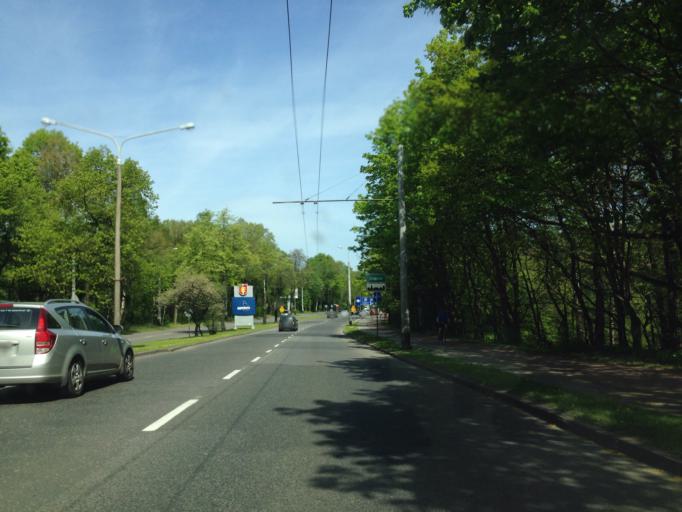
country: PL
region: Pomeranian Voivodeship
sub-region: Sopot
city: Sopot
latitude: 54.4617
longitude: 18.5539
